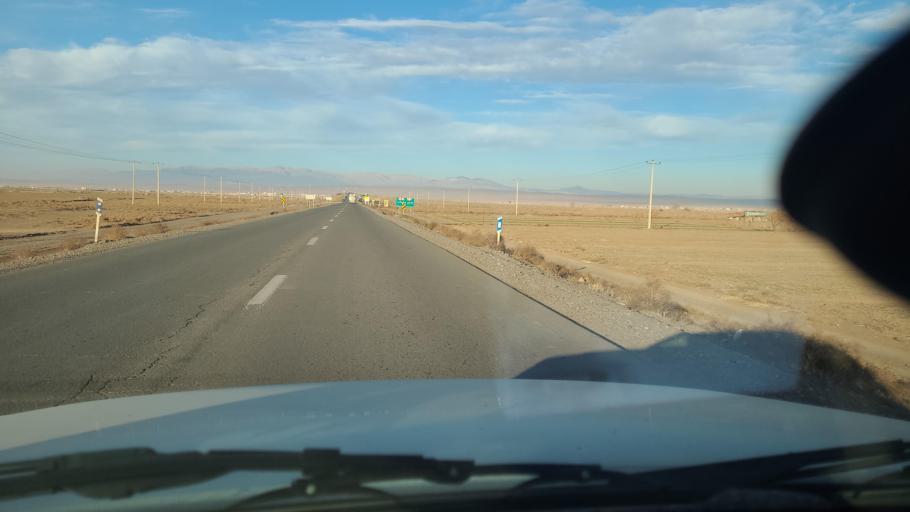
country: IR
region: Razavi Khorasan
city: Neqab
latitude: 36.5963
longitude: 57.5873
